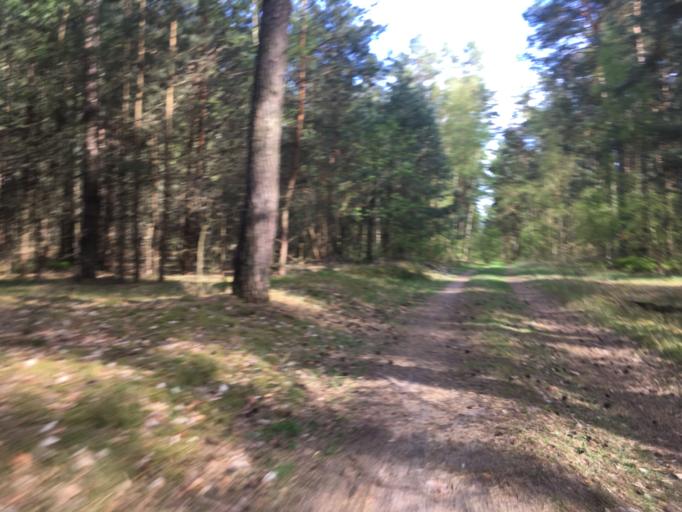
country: DE
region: Brandenburg
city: Bernau bei Berlin
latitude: 52.7138
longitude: 13.5676
